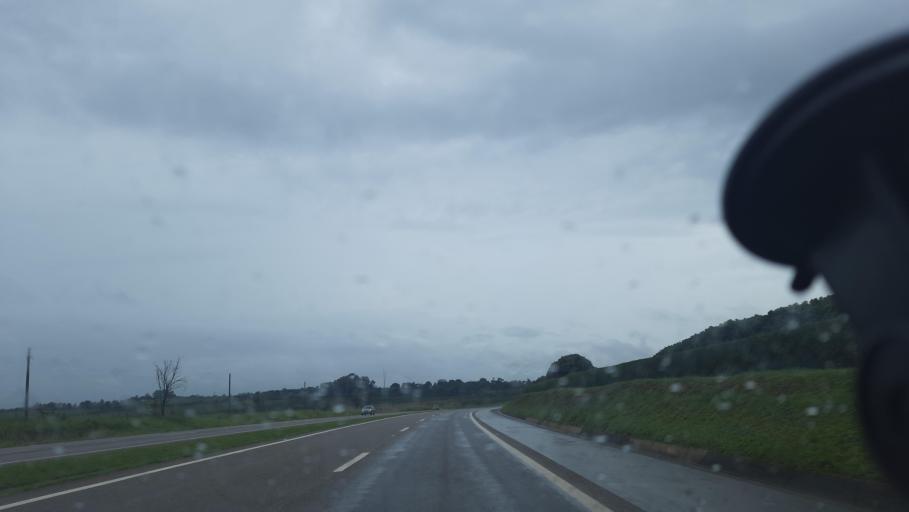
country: BR
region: Sao Paulo
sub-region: Casa Branca
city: Casa Branca
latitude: -21.7974
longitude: -47.0597
